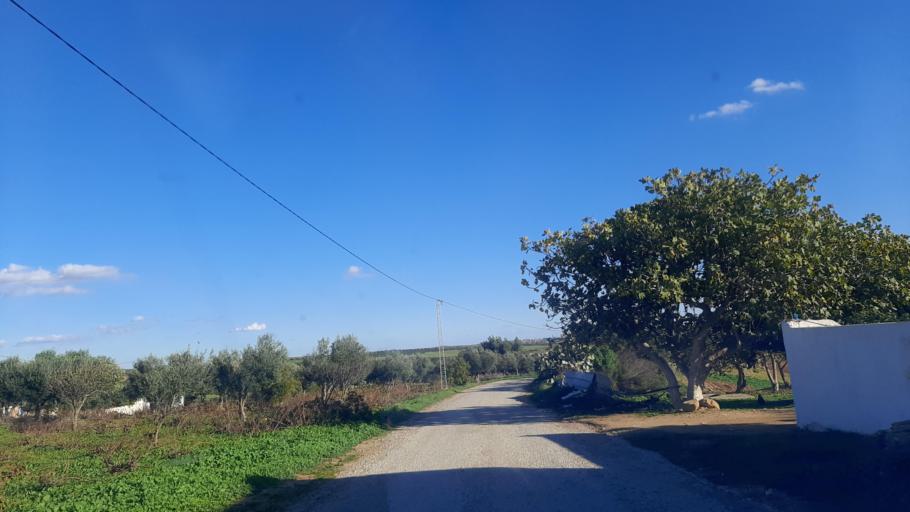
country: TN
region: Nabul
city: El Mida
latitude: 36.8379
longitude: 10.8310
